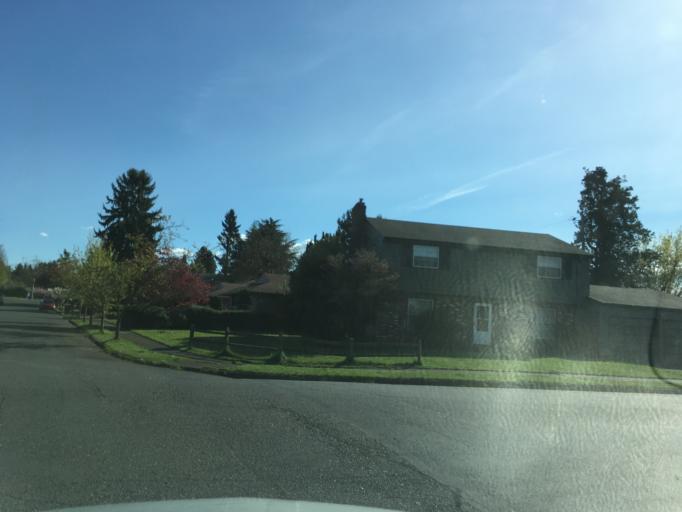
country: US
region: Oregon
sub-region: Multnomah County
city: Fairview
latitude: 45.5403
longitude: -122.5141
